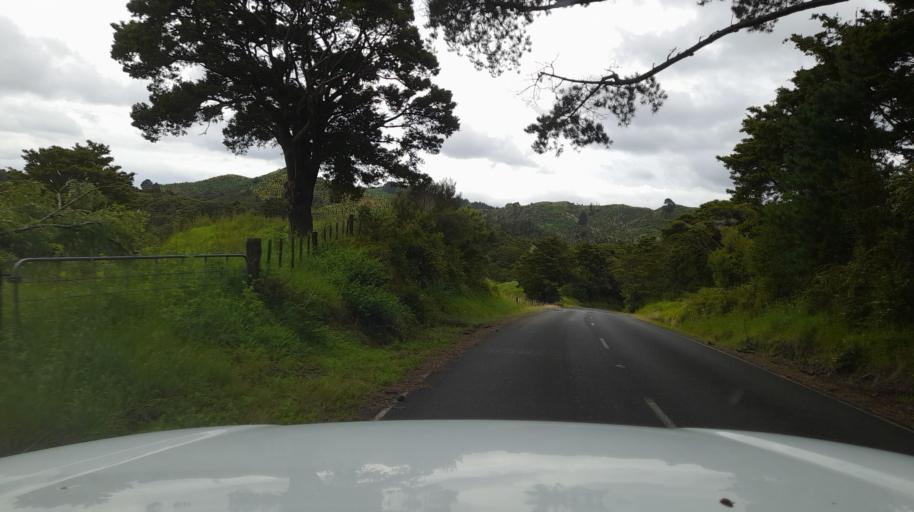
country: NZ
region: Northland
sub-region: Far North District
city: Kaitaia
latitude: -35.2906
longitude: 173.3724
